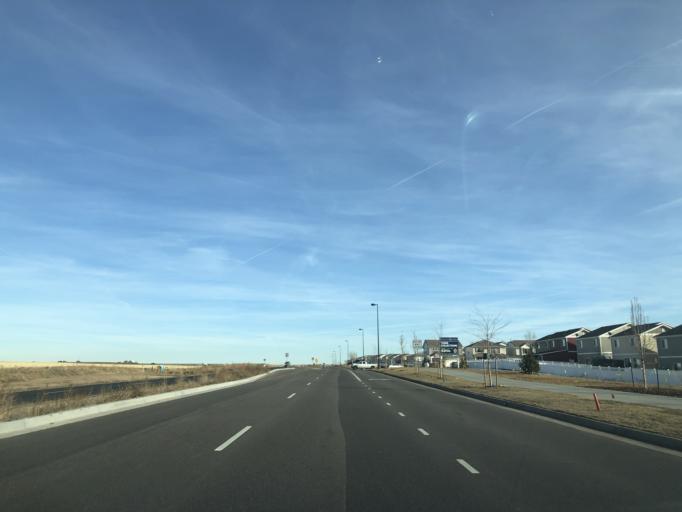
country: US
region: Colorado
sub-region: Adams County
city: Aurora
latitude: 39.7984
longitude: -104.7431
